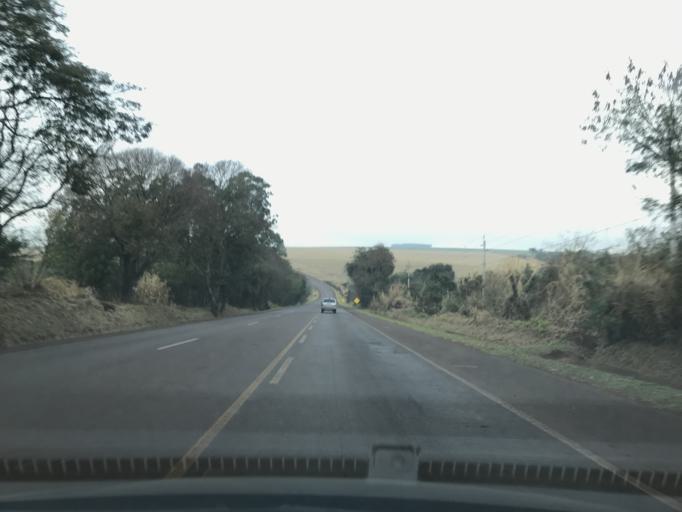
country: BR
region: Parana
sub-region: Toledo
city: Toledo
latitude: -24.6337
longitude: -53.7118
